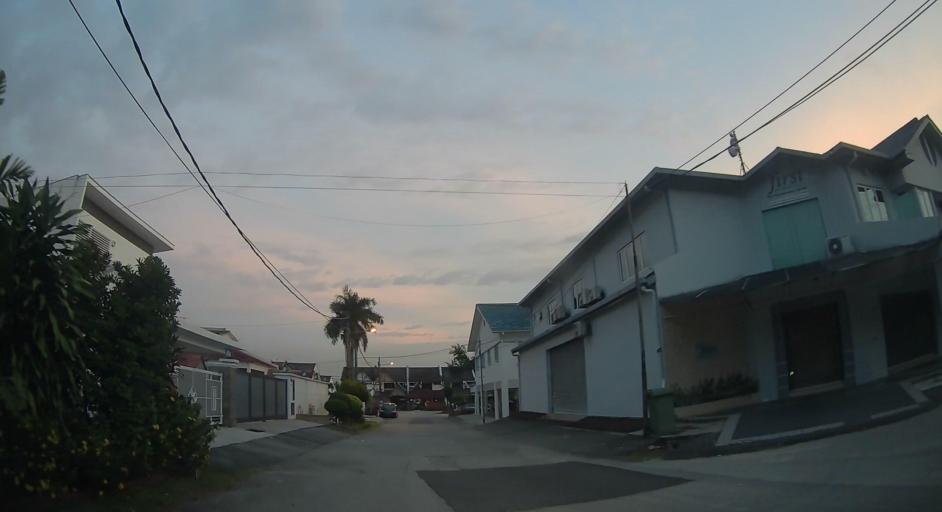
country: MY
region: Selangor
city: Subang Jaya
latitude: 3.0696
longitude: 101.5739
